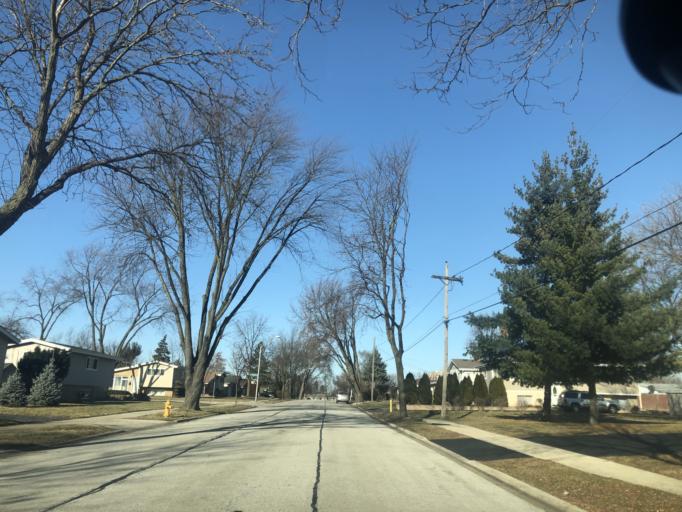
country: US
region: Illinois
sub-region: DuPage County
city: Addison
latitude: 41.9392
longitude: -87.9975
